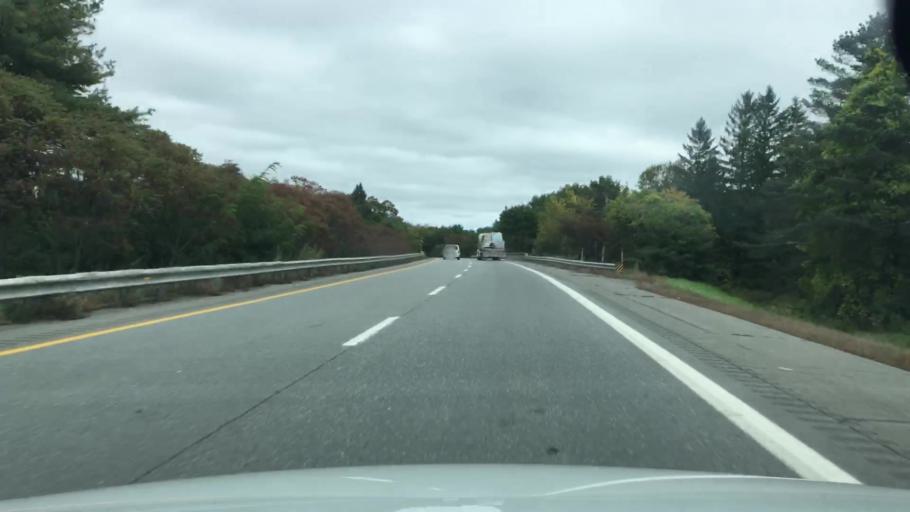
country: US
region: Maine
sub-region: Somerset County
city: Fairfield
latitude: 44.6019
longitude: -69.5845
